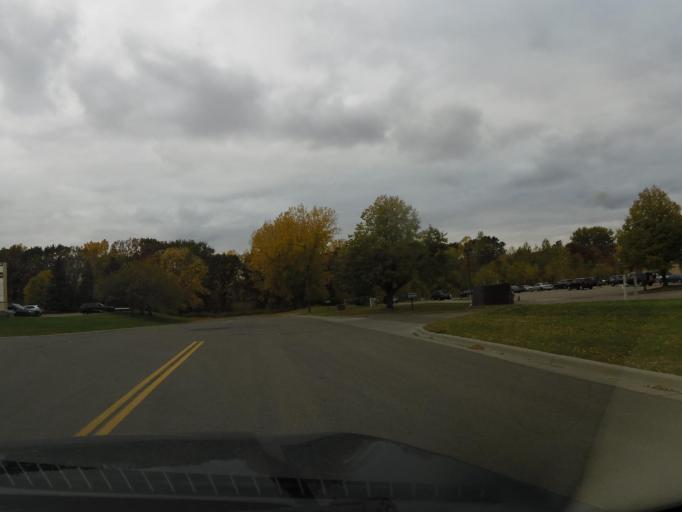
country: US
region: Minnesota
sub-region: Dakota County
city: Lakeville
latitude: 44.6935
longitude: -93.2877
